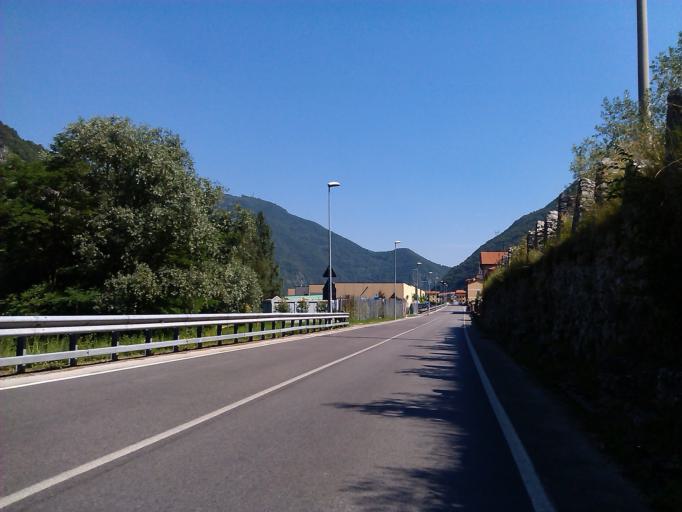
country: IT
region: Veneto
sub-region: Provincia di Vicenza
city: Campolongo sul Brenta
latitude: 45.8324
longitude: 11.6964
